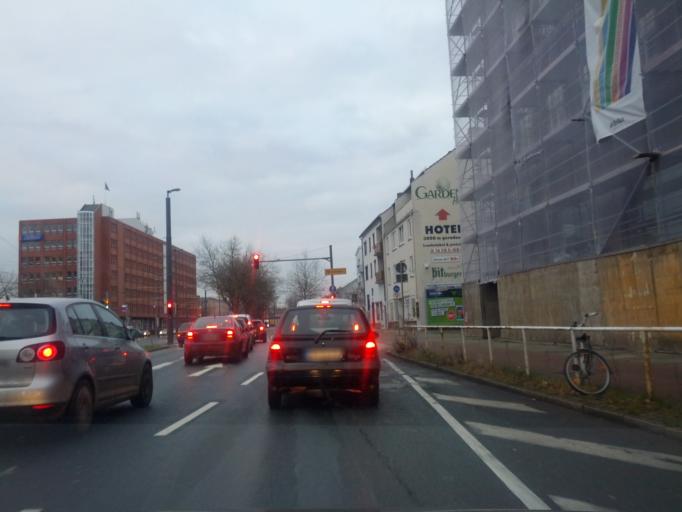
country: DE
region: Bremen
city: Bremen
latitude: 53.0859
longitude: 8.7916
